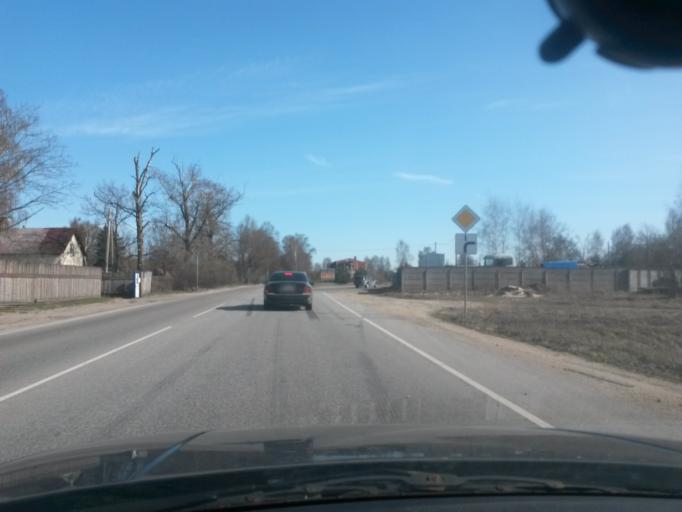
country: LV
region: Kekava
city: Kekava
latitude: 56.8989
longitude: 24.2293
